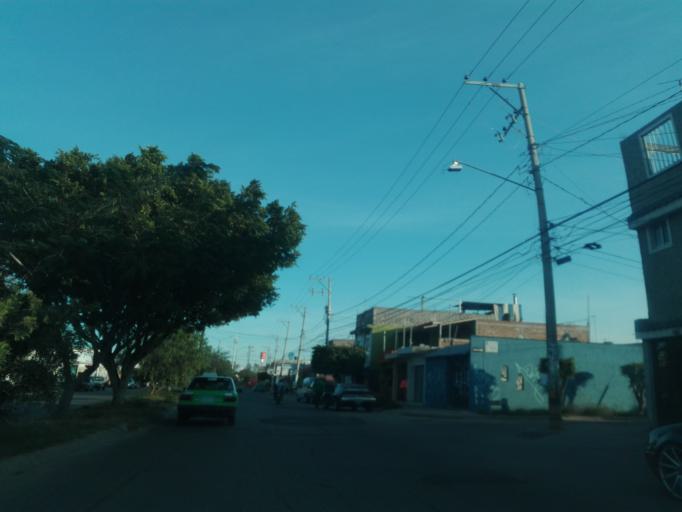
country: MX
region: Guanajuato
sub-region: Leon
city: San Jose de Duran (Los Troncoso)
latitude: 21.0861
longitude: -101.6465
